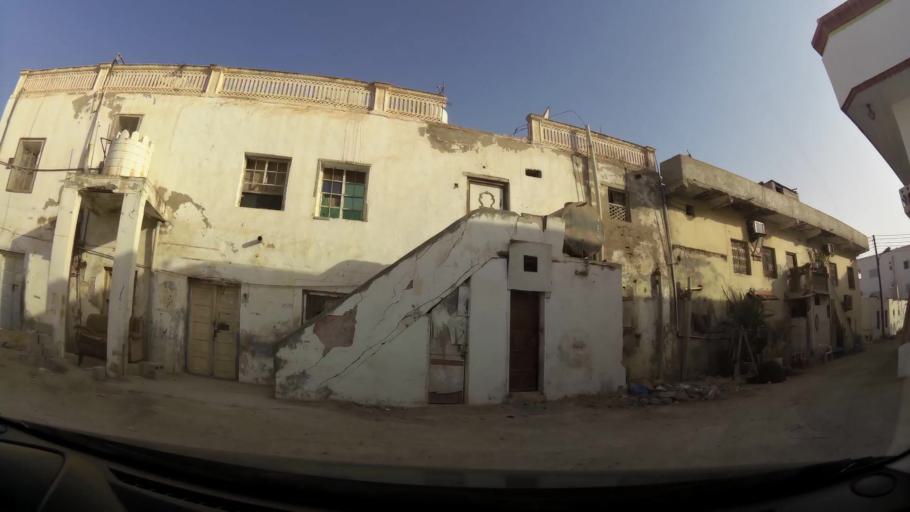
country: OM
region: Zufar
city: Salalah
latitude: 17.0101
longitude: 54.0868
